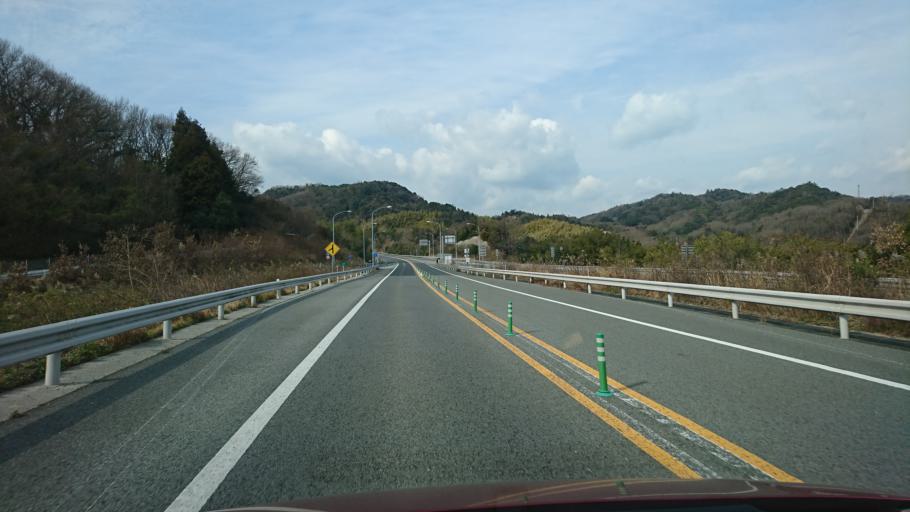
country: JP
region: Hiroshima
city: Innoshima
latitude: 34.1292
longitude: 133.0329
